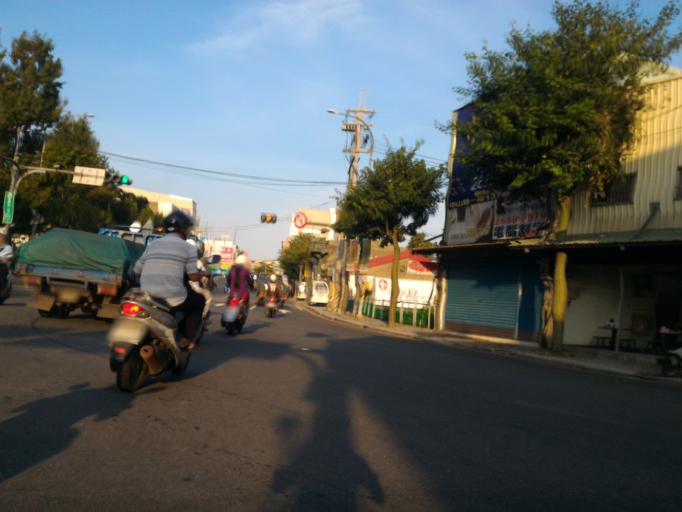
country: TW
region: Taiwan
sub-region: Taoyuan
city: Taoyuan
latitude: 24.9563
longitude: 121.3897
